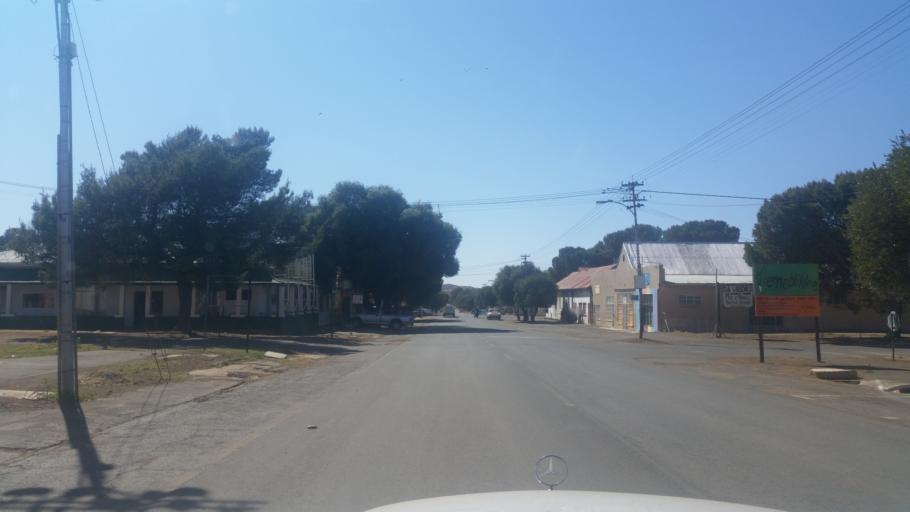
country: ZA
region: Orange Free State
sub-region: Xhariep District Municipality
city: Trompsburg
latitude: -30.4954
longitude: 25.9736
